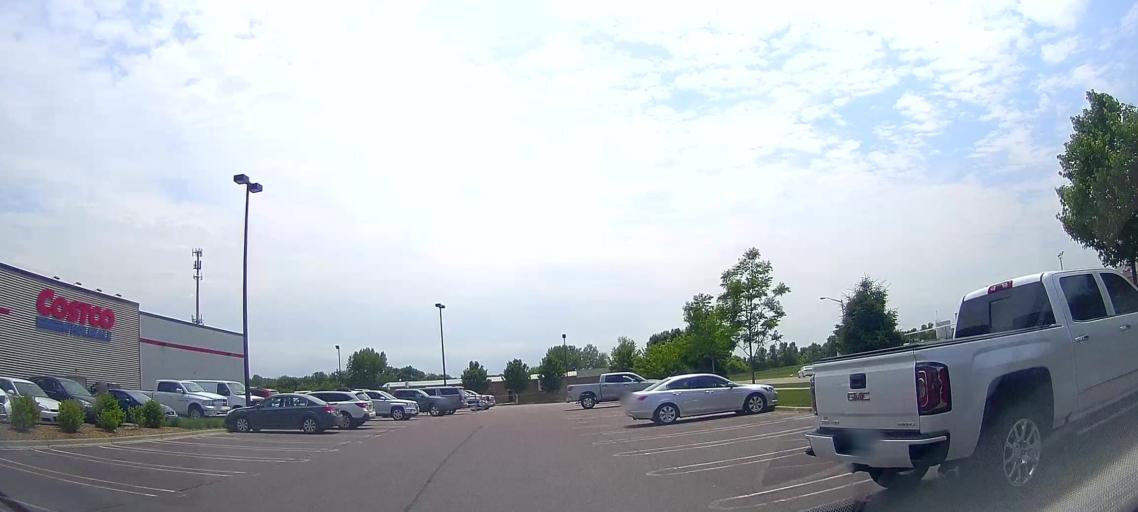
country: US
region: South Dakota
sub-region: Minnehaha County
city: Sioux Falls
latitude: 43.5122
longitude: -96.7405
